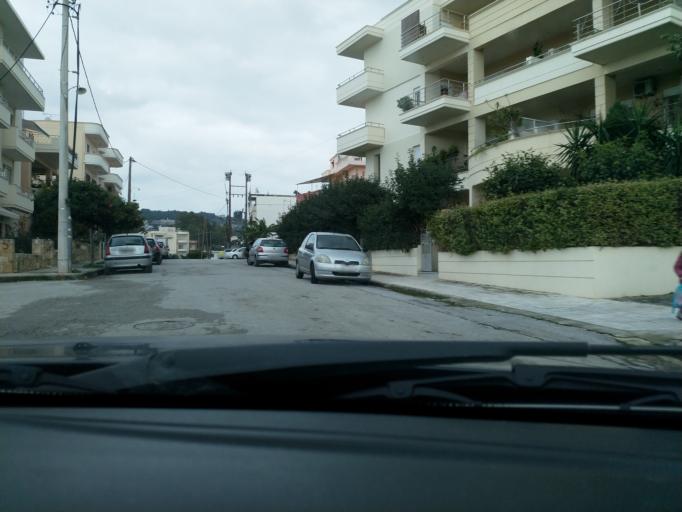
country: GR
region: Crete
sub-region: Nomos Chanias
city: Chania
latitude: 35.5112
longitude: 24.0391
